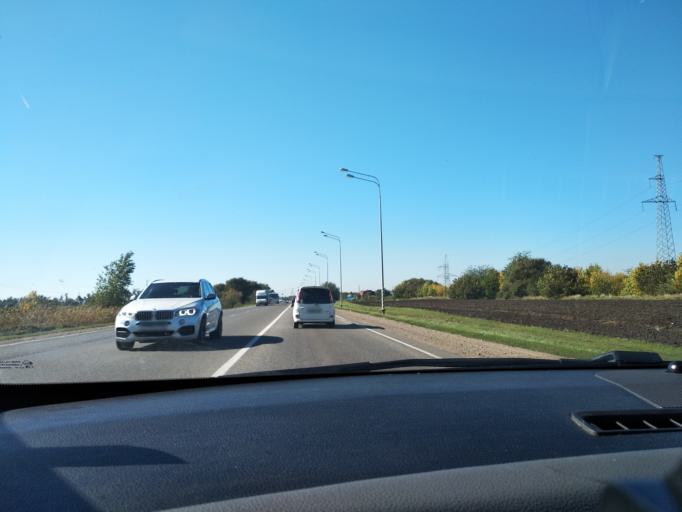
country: RU
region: Krasnodarskiy
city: Agronom
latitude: 45.1703
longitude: 39.0941
